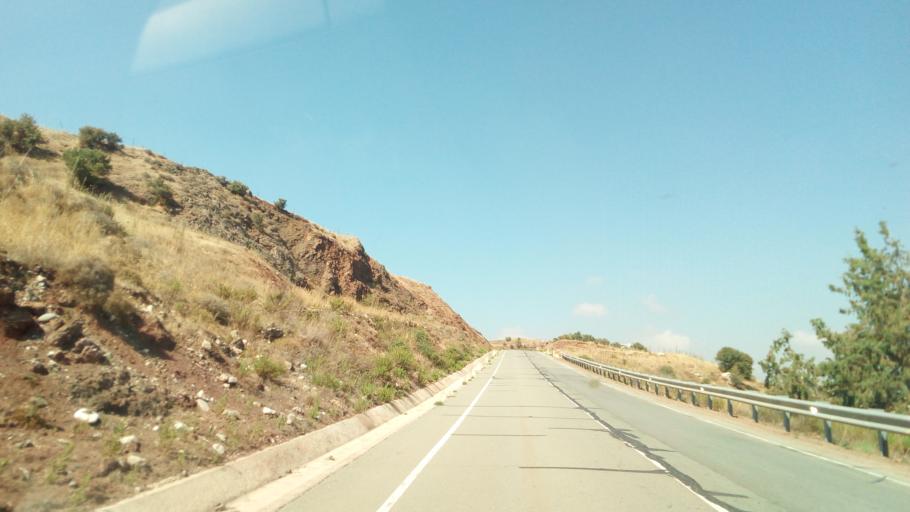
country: CY
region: Limassol
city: Pissouri
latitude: 34.7729
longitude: 32.6067
